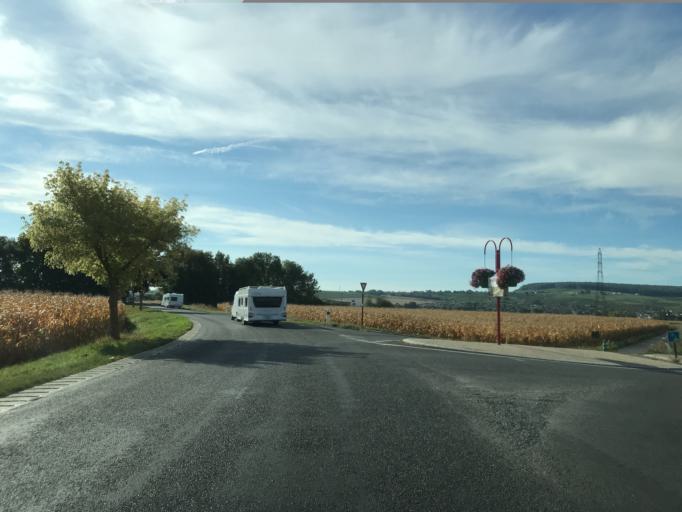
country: FR
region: Champagne-Ardenne
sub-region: Departement de la Marne
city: Mardeuil
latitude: 49.0695
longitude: 3.9318
